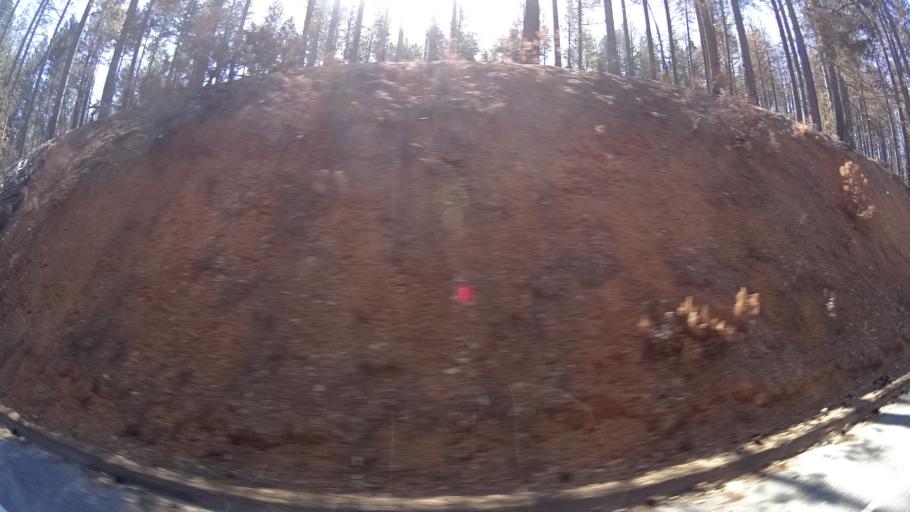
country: US
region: California
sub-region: Tehama County
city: Rancho Tehama Reserve
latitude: 39.6562
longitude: -122.7263
